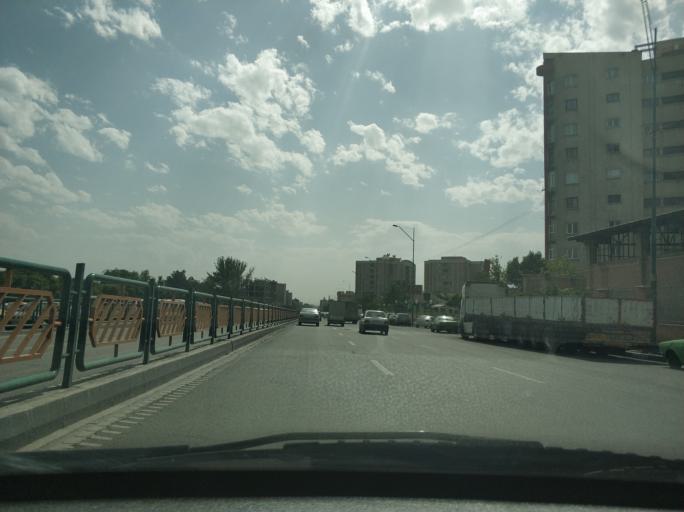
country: IR
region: Tehran
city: Tehran
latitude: 35.7228
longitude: 51.5164
